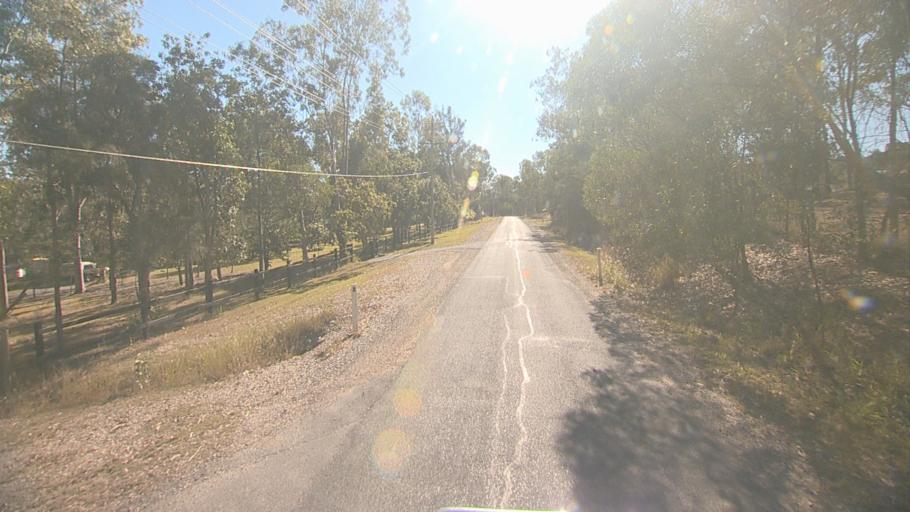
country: AU
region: Queensland
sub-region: Logan
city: Chambers Flat
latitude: -27.7729
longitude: 153.1418
